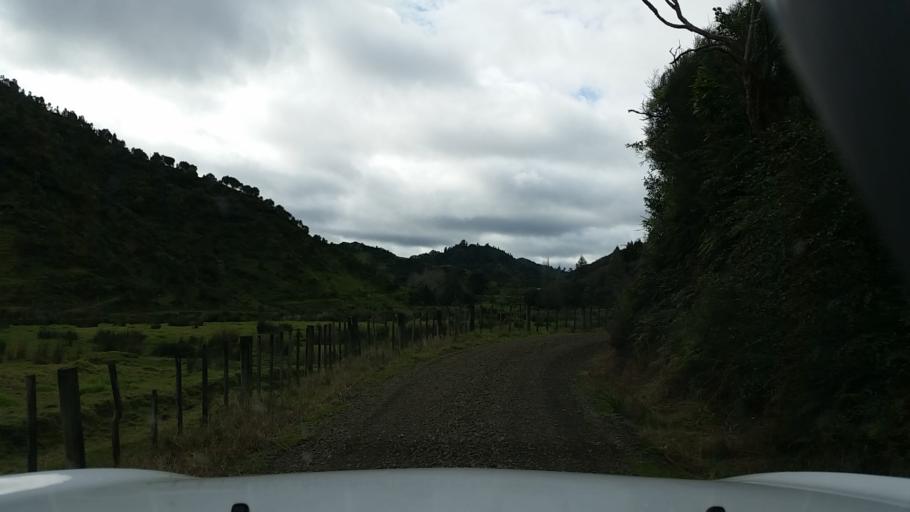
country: NZ
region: Taranaki
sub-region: New Plymouth District
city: Waitara
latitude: -38.8540
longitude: 174.6726
